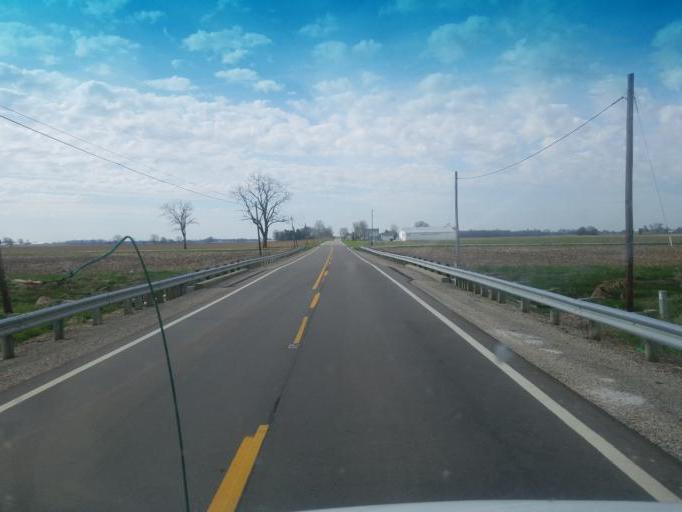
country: US
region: Ohio
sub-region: Marion County
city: Prospect
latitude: 40.4195
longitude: -83.1746
